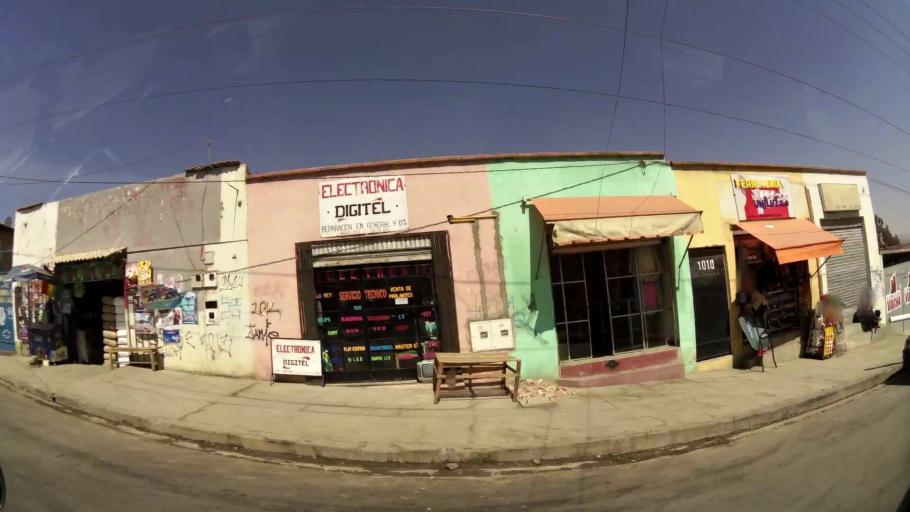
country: BO
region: La Paz
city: La Paz
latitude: -16.5343
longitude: -68.0406
